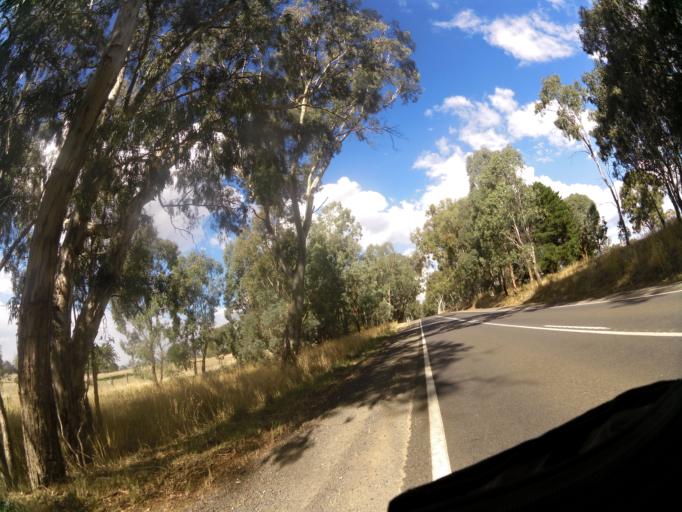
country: AU
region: Victoria
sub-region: Mansfield
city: Mansfield
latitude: -36.9965
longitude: 146.0601
